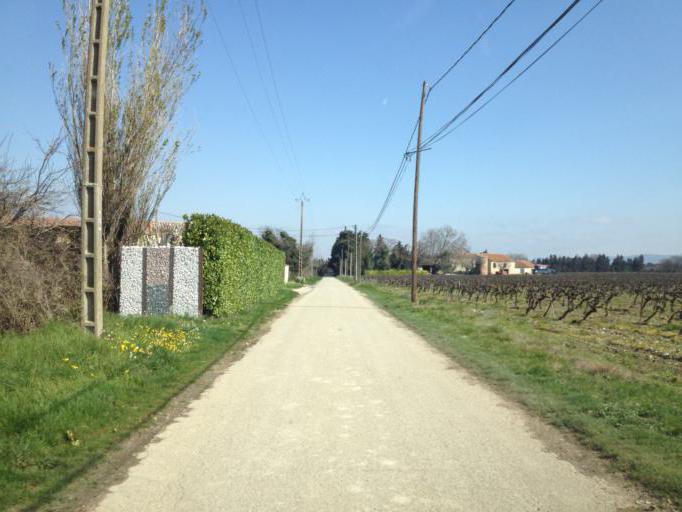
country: FR
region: Provence-Alpes-Cote d'Azur
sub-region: Departement du Vaucluse
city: Jonquieres
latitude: 44.1279
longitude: 4.9156
